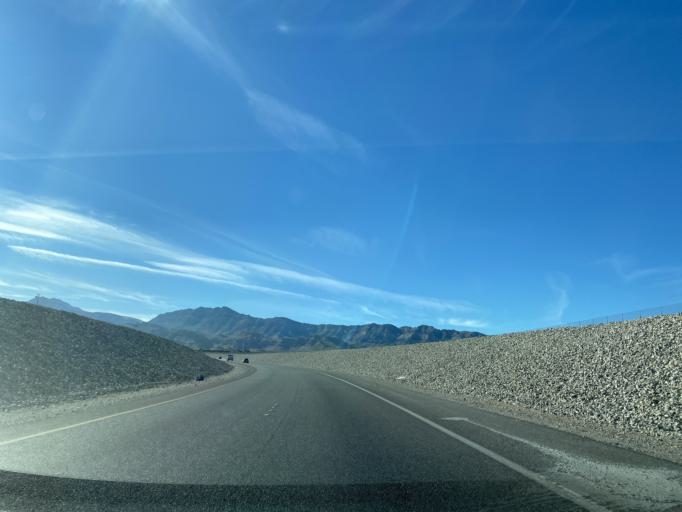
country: US
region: Nevada
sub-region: Clark County
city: Summerlin South
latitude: 36.2826
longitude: -115.3171
